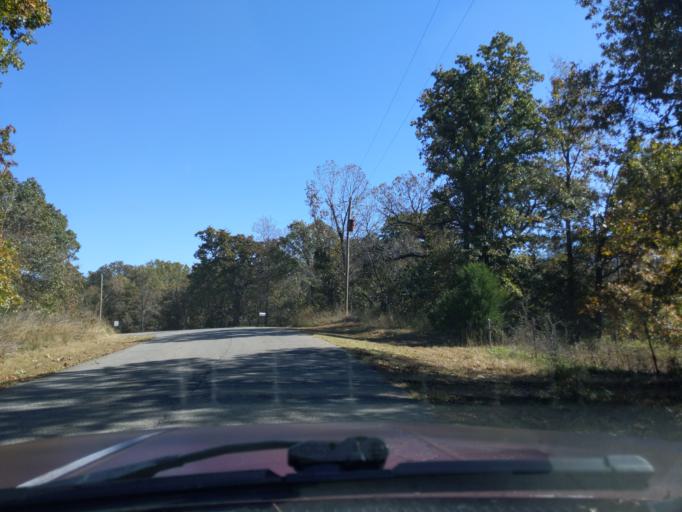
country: US
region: Oklahoma
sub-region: Creek County
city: Bristow
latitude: 35.7048
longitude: -96.4069
